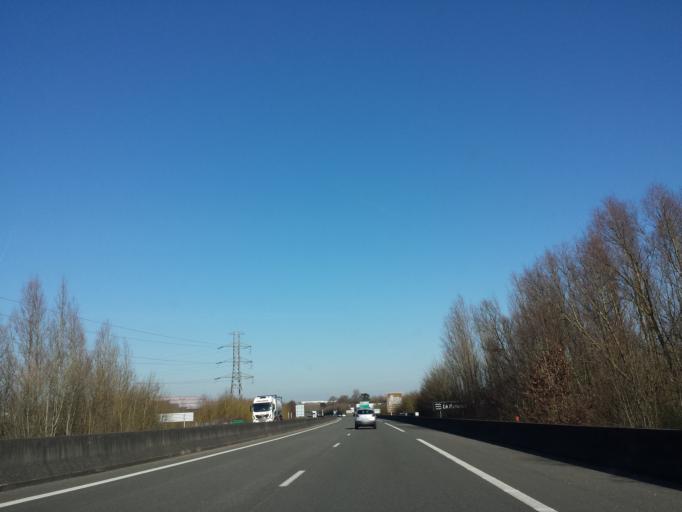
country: FR
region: Picardie
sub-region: Departement de l'Oise
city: Allonne
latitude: 49.4089
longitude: 2.1267
